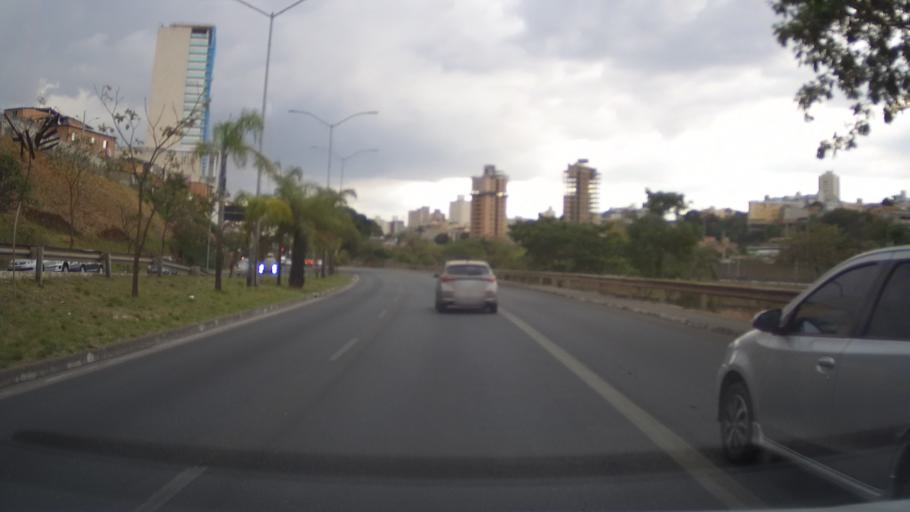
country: BR
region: Minas Gerais
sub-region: Belo Horizonte
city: Belo Horizonte
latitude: -19.9197
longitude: -43.9173
